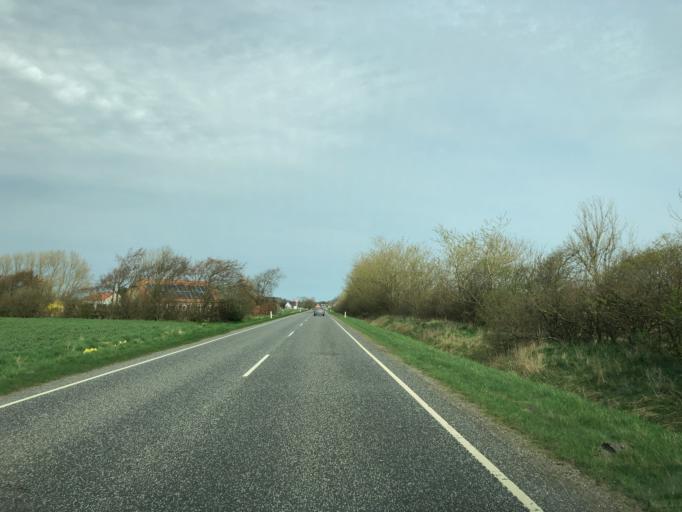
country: DK
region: Central Jutland
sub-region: Ringkobing-Skjern Kommune
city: Skjern
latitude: 55.8973
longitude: 8.4273
